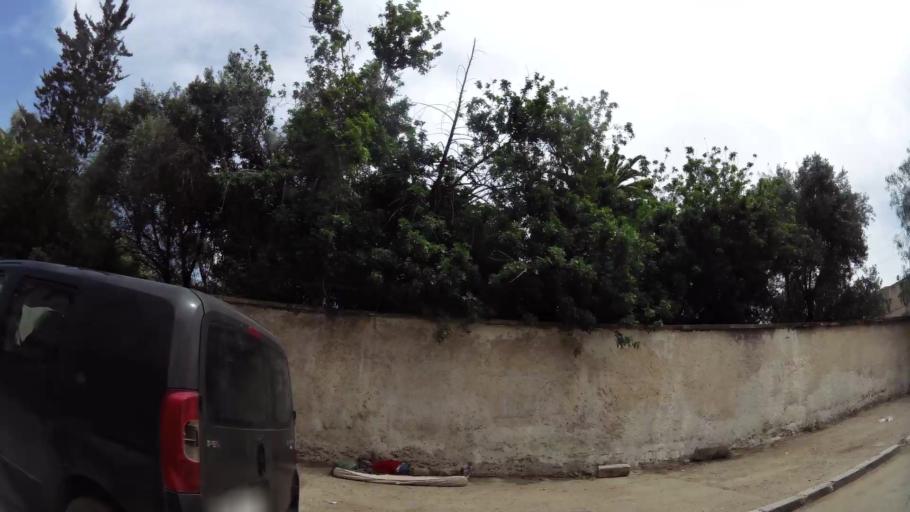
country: MA
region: Rabat-Sale-Zemmour-Zaer
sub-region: Khemisset
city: Khemisset
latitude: 33.8233
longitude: -6.0666
